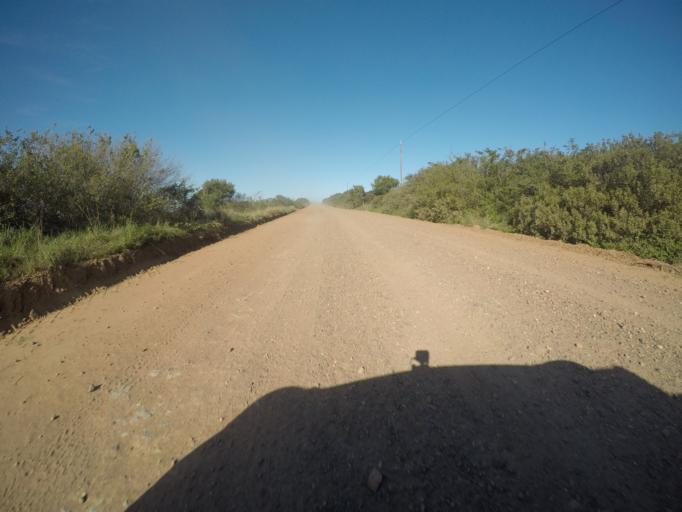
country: ZA
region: Western Cape
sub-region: Eden District Municipality
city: Mossel Bay
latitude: -34.1448
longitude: 22.0097
